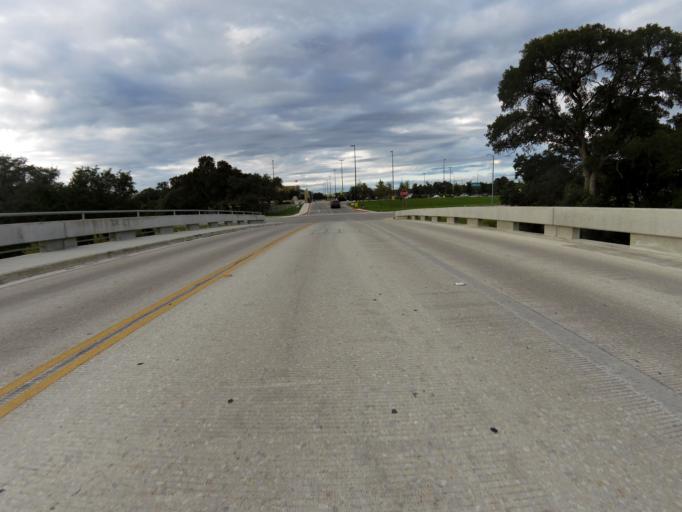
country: US
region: Texas
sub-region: Bexar County
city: Cross Mountain
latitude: 29.6672
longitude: -98.6342
